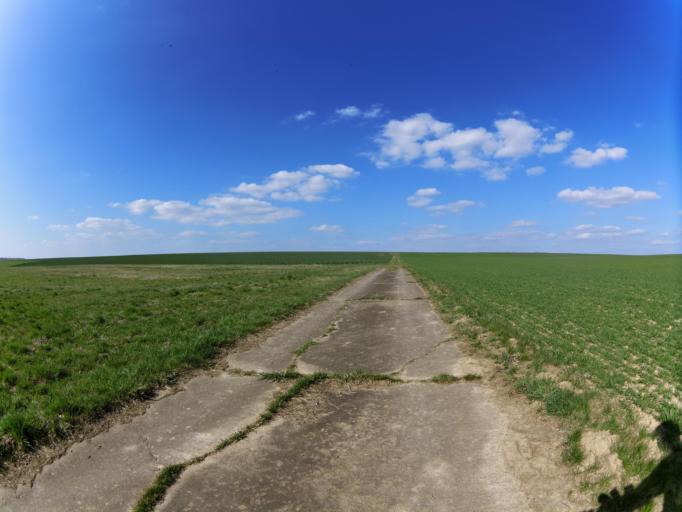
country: DE
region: Bavaria
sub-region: Regierungsbezirk Unterfranken
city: Dettelbach
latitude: 49.8337
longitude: 10.1614
